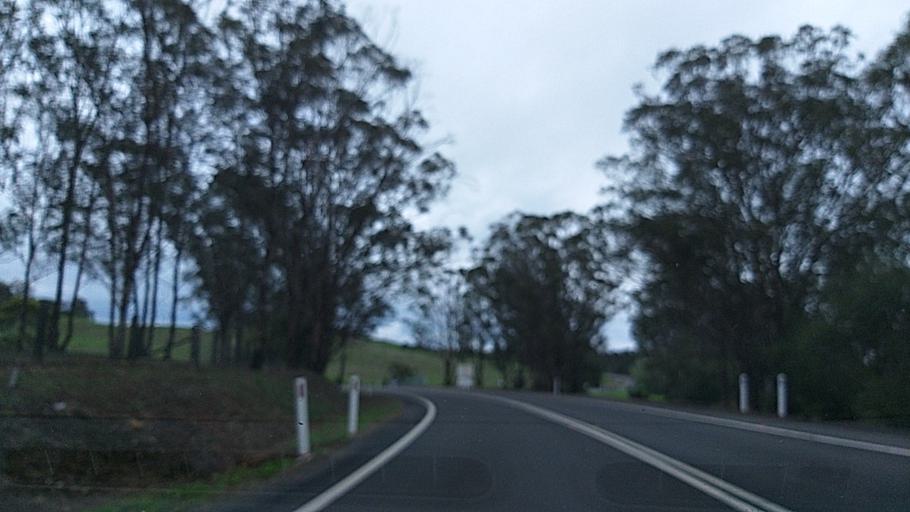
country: AU
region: New South Wales
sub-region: Camden
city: Camden South
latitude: -34.1232
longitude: 150.6995
